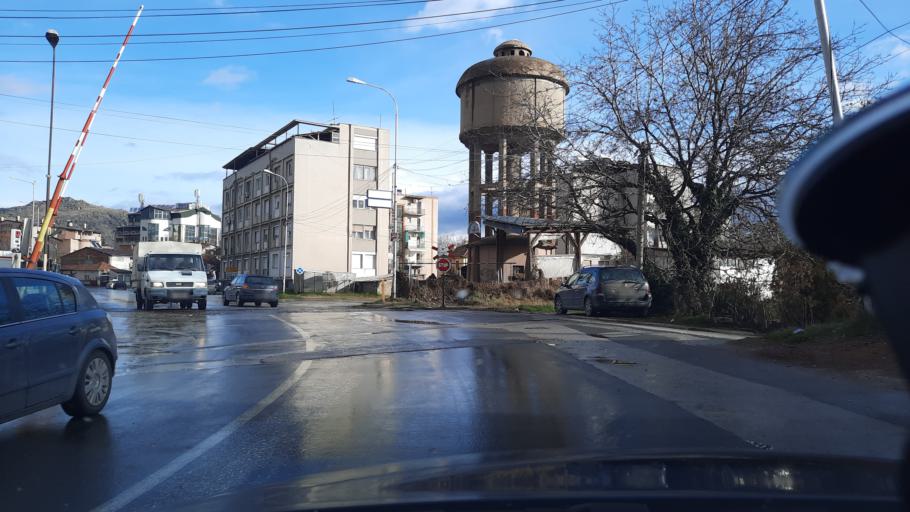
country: MK
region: Prilep
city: Prilep
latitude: 41.3432
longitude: 21.5409
